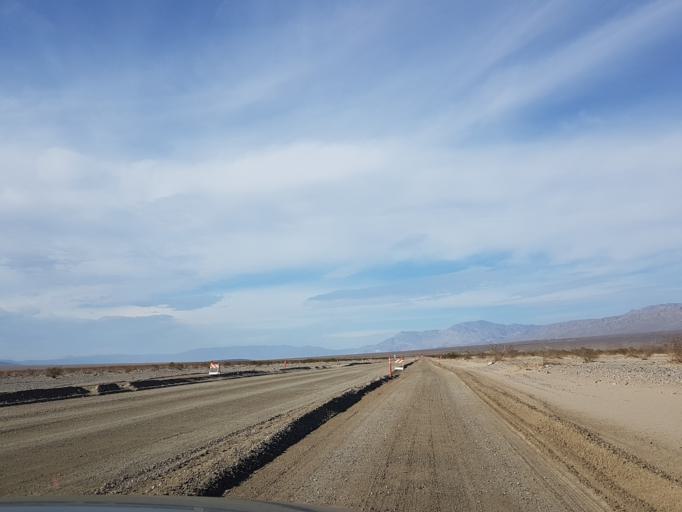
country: US
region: California
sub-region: San Bernardino County
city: Searles Valley
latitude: 36.1479
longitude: -117.2972
